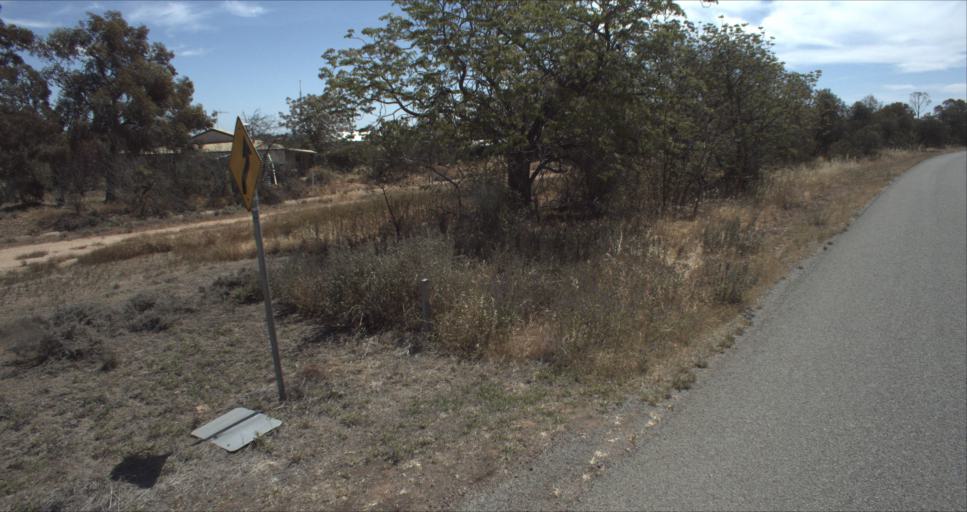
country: AU
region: New South Wales
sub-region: Leeton
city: Leeton
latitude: -34.5854
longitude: 146.4301
